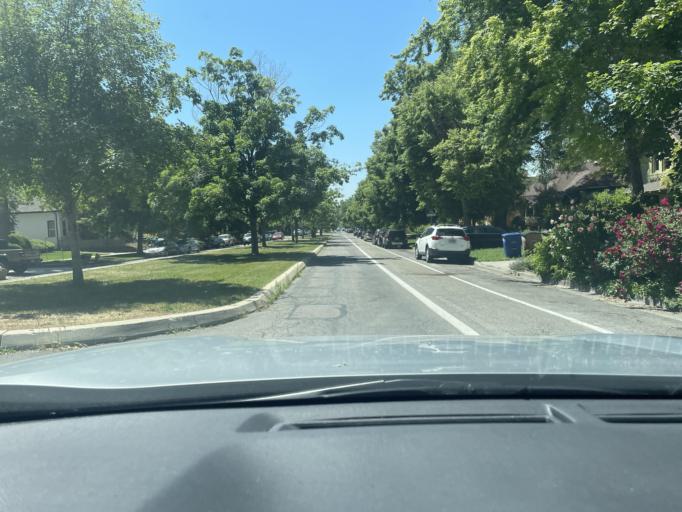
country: US
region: Utah
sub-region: Salt Lake County
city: Salt Lake City
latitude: 40.7643
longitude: -111.8740
